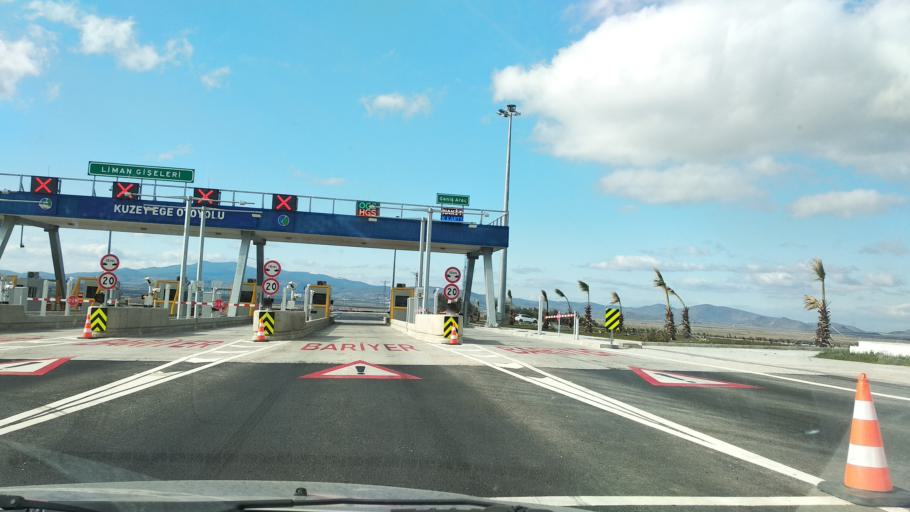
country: TR
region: Izmir
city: Zeytindag
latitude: 38.9734
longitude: 27.0541
